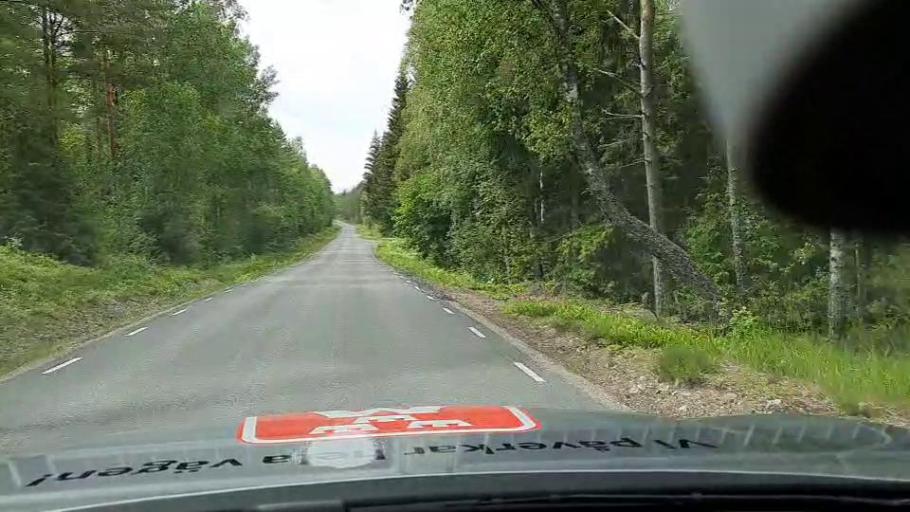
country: SE
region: Soedermanland
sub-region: Eskilstuna Kommun
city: Arla
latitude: 59.2314
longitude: 16.7426
